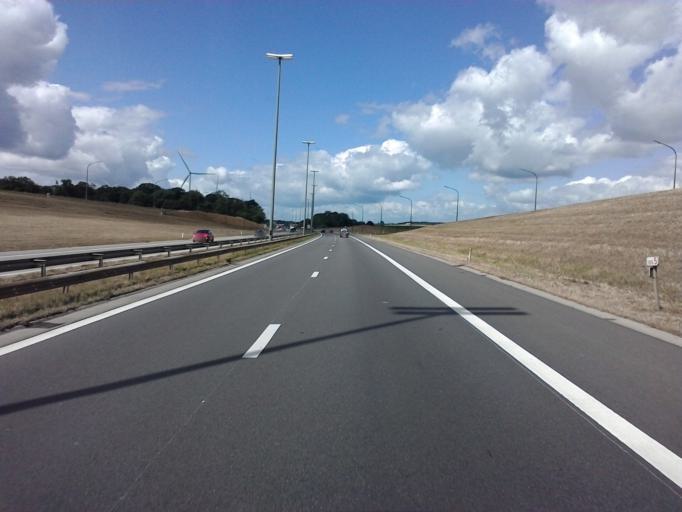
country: LU
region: Luxembourg
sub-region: Canton de Capellen
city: Steinfort
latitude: 49.6403
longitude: 5.8876
